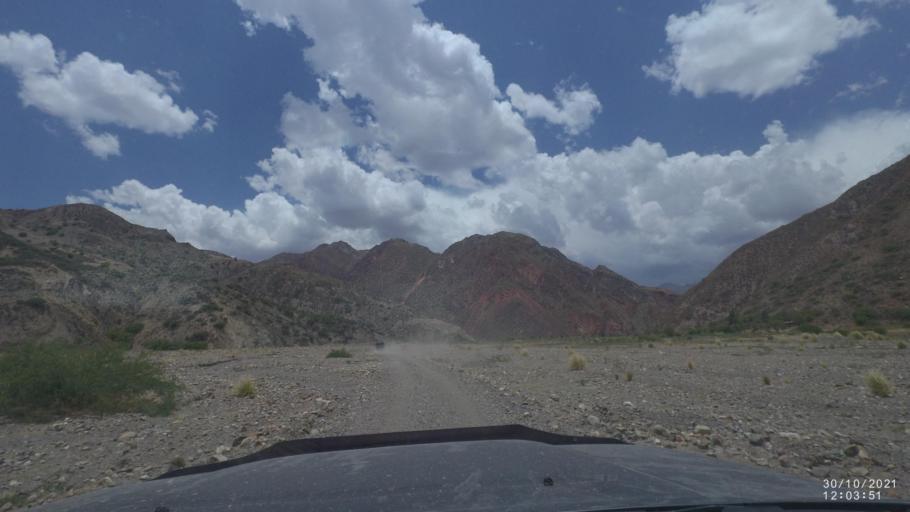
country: BO
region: Cochabamba
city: Colchani
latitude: -17.5283
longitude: -66.6201
